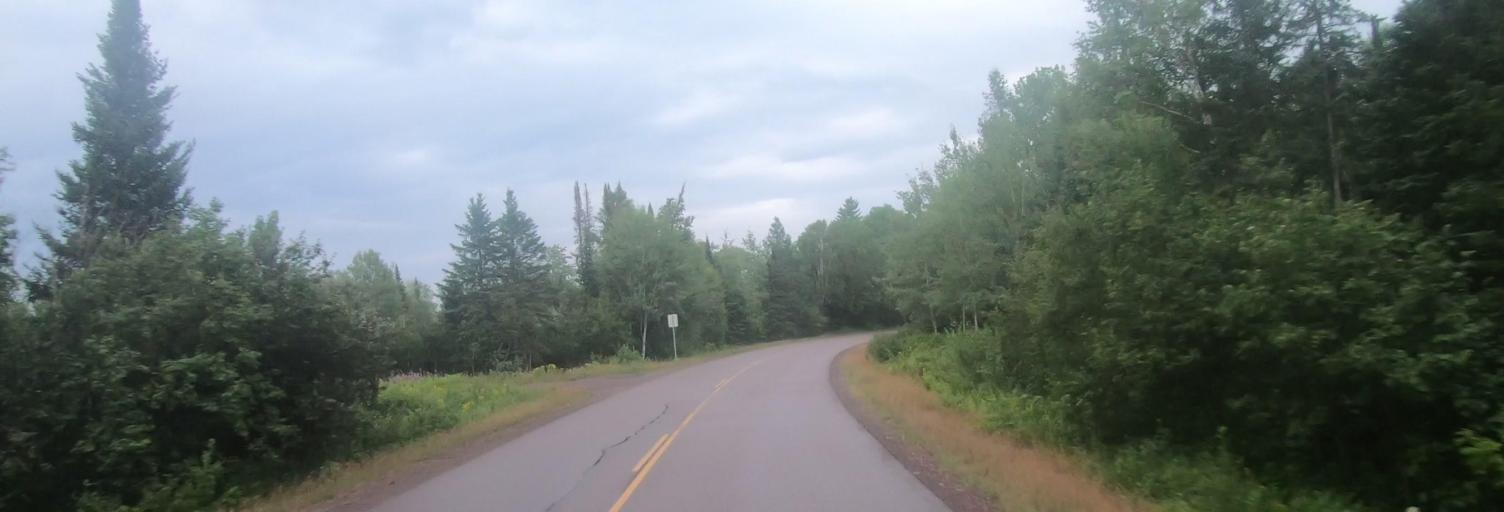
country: US
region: Michigan
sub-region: Keweenaw County
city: Eagle River
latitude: 47.2856
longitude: -88.2842
